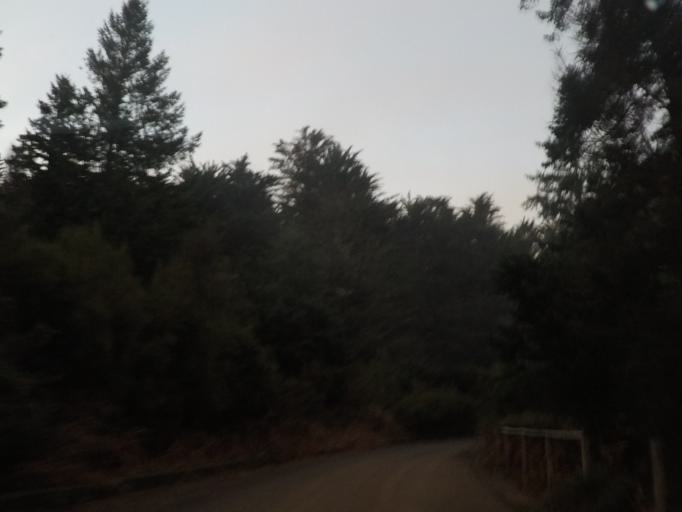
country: PT
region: Madeira
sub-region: Santa Cruz
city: Camacha
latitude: 32.7141
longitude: -16.8547
